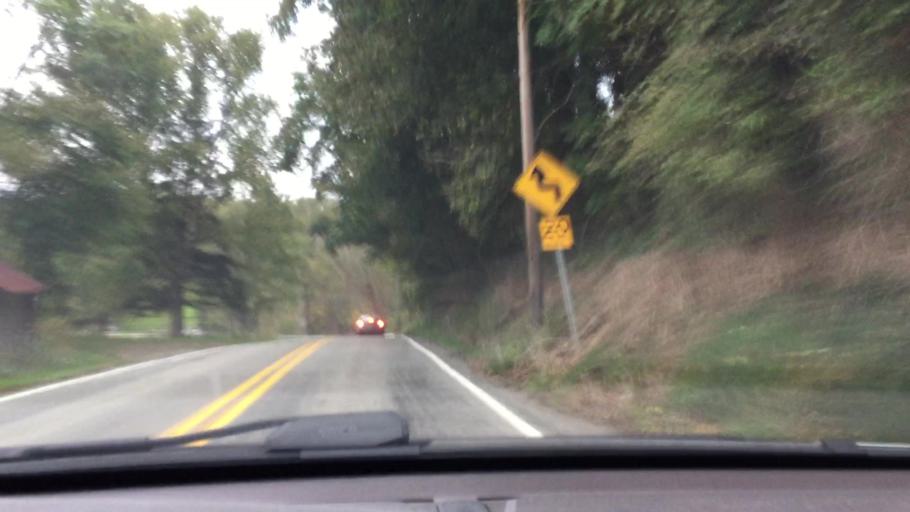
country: US
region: Pennsylvania
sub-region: Washington County
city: McMurray
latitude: 40.1867
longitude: -80.1023
